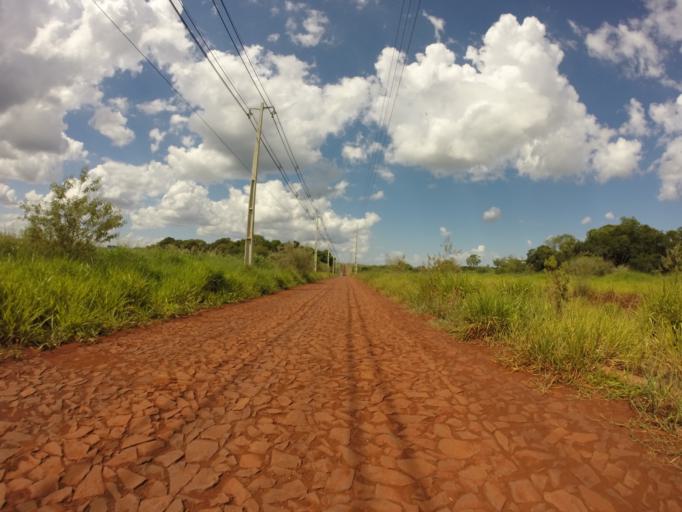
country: PY
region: Alto Parana
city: Ciudad del Este
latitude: -25.3207
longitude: -54.6824
